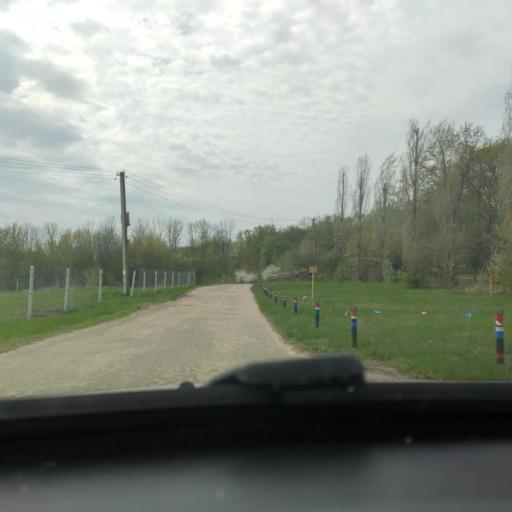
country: RU
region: Voronezj
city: Podgornoye
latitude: 51.7577
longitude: 39.0805
